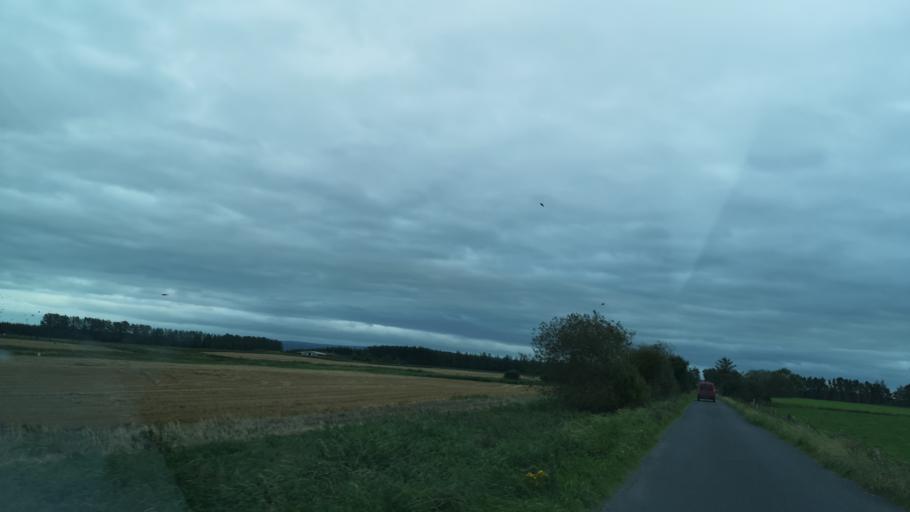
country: IE
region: Leinster
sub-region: Uibh Fhaili
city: Ferbane
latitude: 53.2132
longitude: -7.7248
